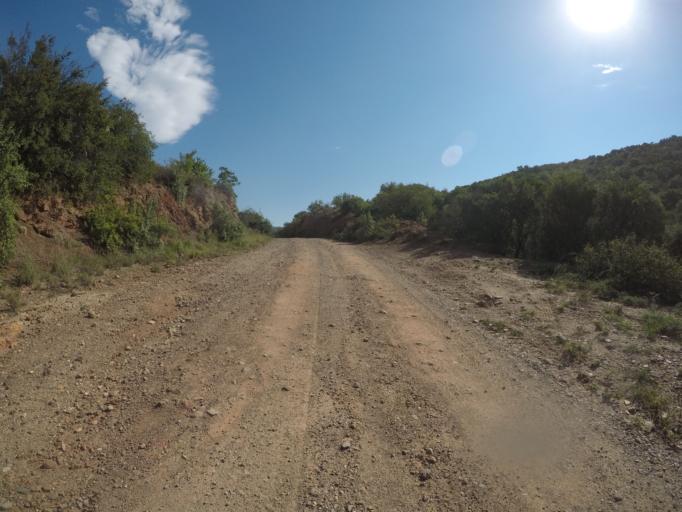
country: ZA
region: Eastern Cape
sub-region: Cacadu District Municipality
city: Kareedouw
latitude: -33.6547
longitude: 24.4246
